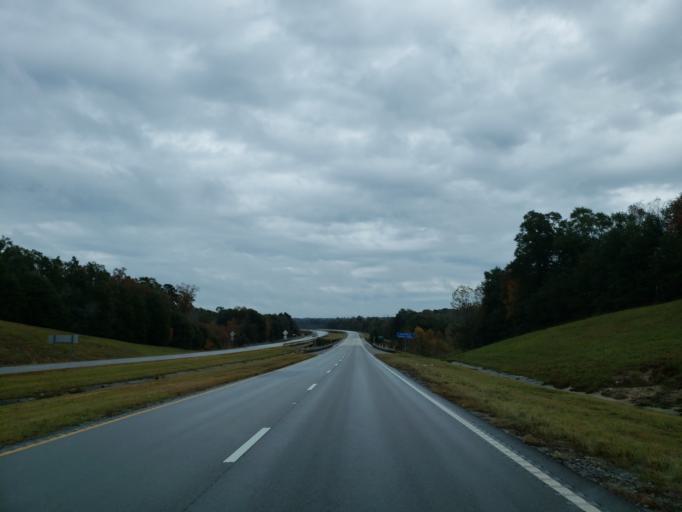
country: US
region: Mississippi
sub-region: Wayne County
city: Waynesboro
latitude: 31.6824
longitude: -88.6859
